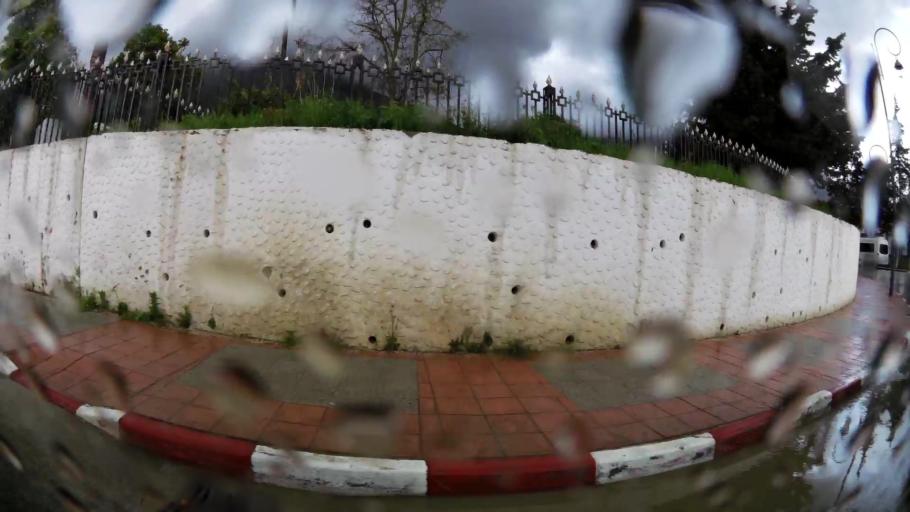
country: MA
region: Tanger-Tetouan
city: Chefchaouene
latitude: 35.1706
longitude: -5.2730
